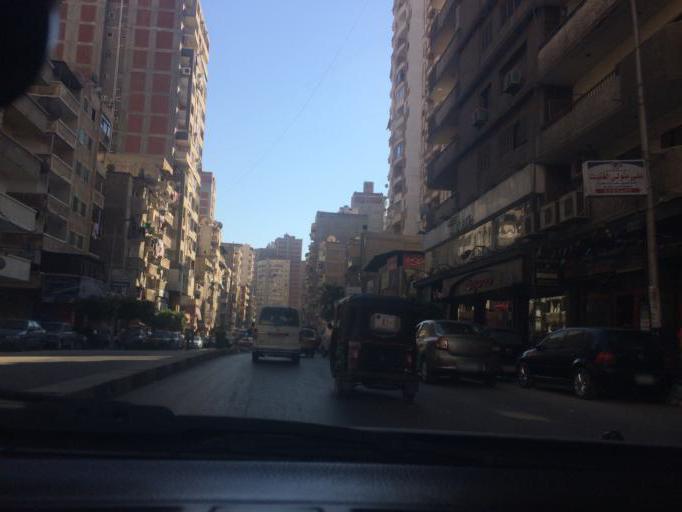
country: EG
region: Alexandria
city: Alexandria
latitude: 31.2577
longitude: 29.9873
